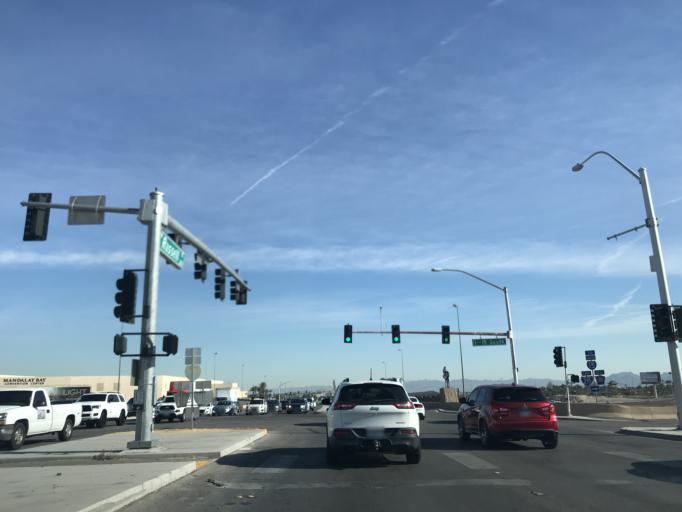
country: US
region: Nevada
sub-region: Clark County
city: Paradise
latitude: 36.0860
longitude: -115.1824
